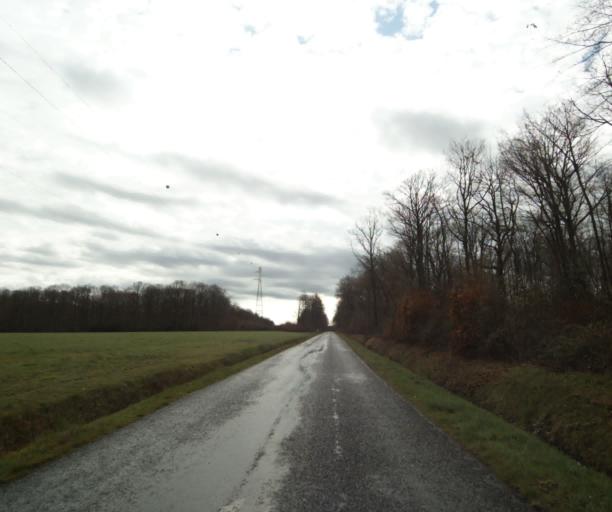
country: FR
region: Auvergne
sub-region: Departement de l'Allier
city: Neuilly-le-Real
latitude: 46.5182
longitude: 3.4350
